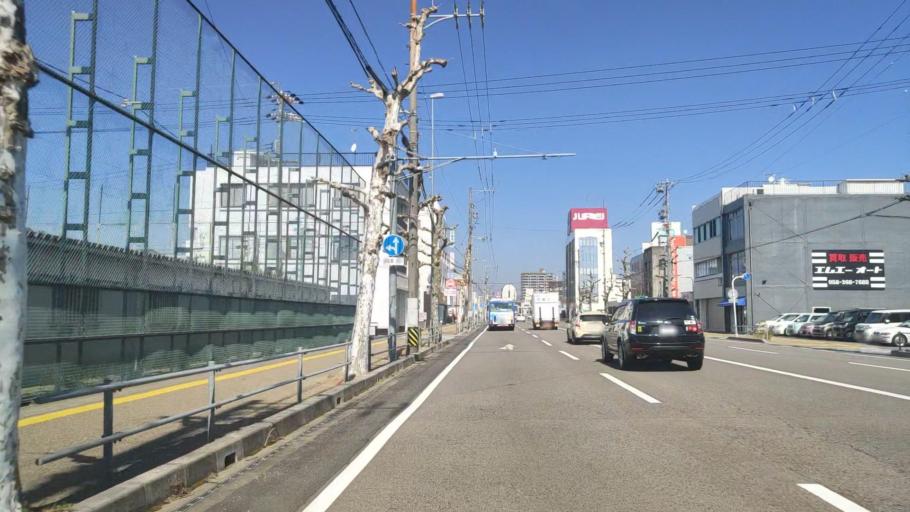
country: JP
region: Gifu
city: Gifu-shi
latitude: 35.4049
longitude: 136.7474
